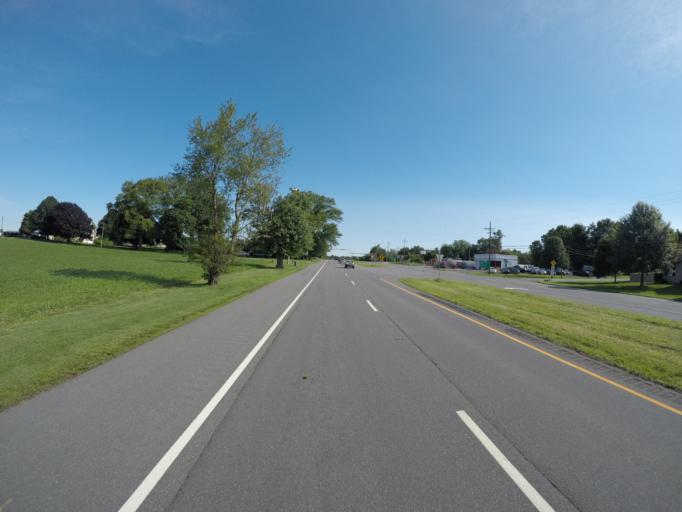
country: US
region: Delaware
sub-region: New Castle County
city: Bear
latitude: 39.5627
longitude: -75.6538
